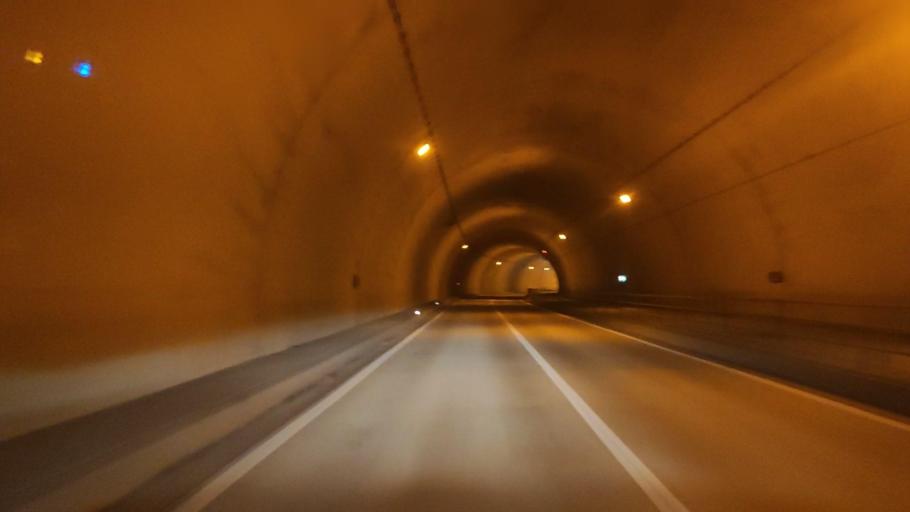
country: JP
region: Kumamoto
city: Hitoyoshi
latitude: 32.3889
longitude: 130.8339
